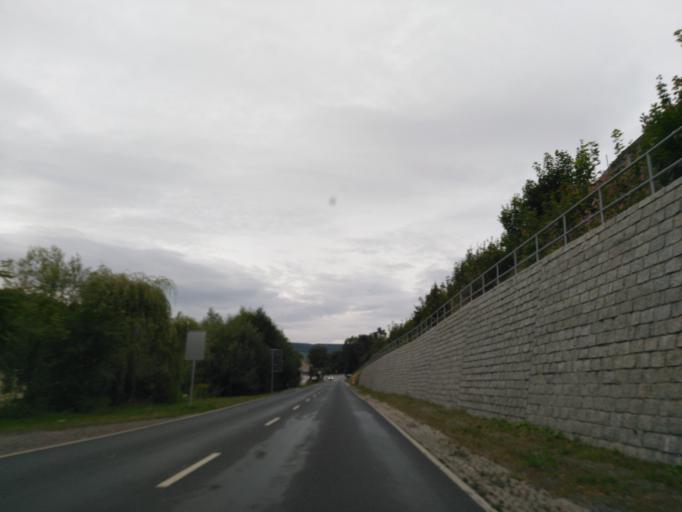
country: DE
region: Saxony
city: Schwarzenberg
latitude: 50.5390
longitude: 12.7974
